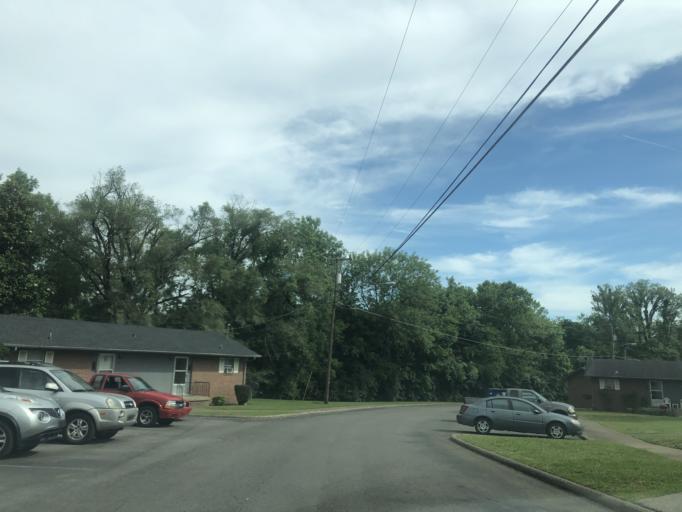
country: US
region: Tennessee
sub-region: Davidson County
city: Nashville
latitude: 36.2206
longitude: -86.8057
